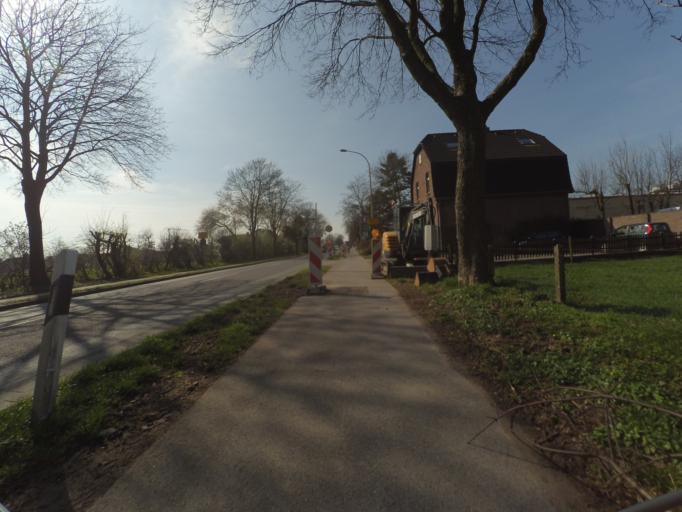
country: DE
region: North Rhine-Westphalia
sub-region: Regierungsbezirk Dusseldorf
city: Kleve
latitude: 51.8023
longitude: 6.1702
